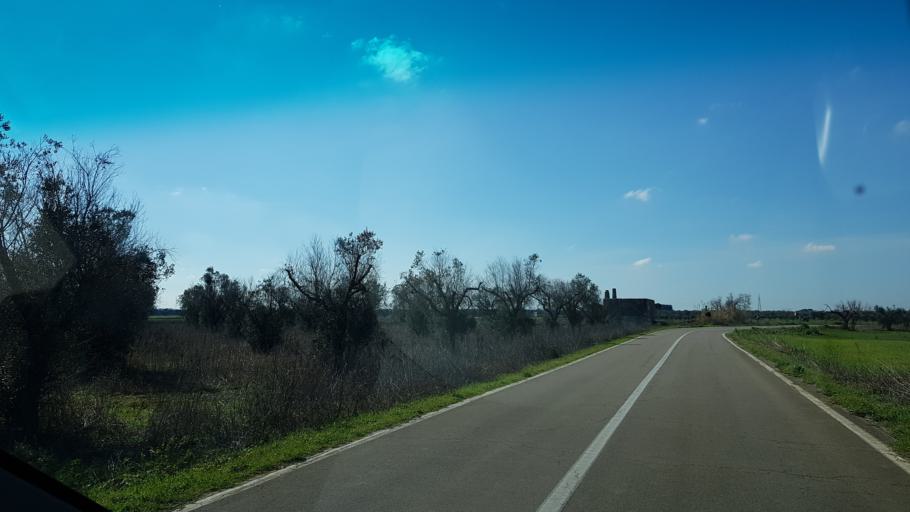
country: IT
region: Apulia
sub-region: Provincia di Brindisi
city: Cellino San Marco
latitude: 40.4407
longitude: 17.9961
